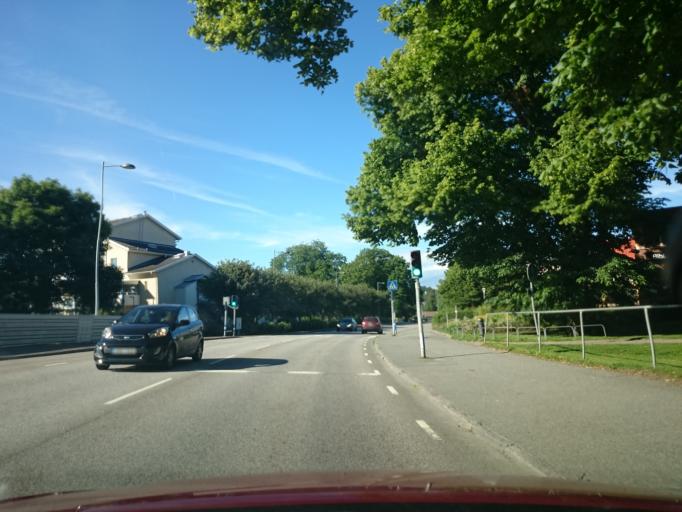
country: SE
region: Vaestra Goetaland
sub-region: Lerums Kommun
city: Lerum
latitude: 57.7731
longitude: 12.2741
